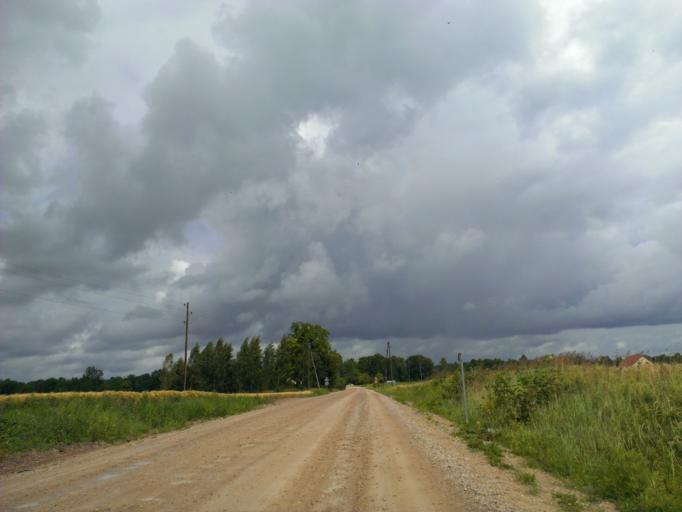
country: LV
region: Sigulda
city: Sigulda
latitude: 57.1947
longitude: 24.9447
